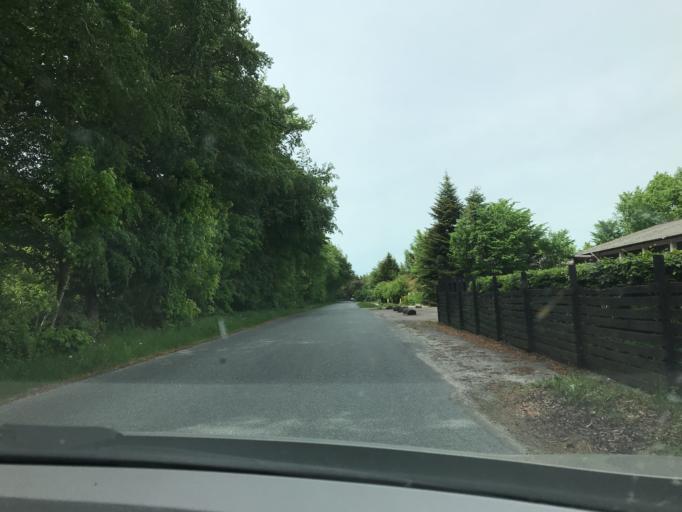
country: DK
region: Central Jutland
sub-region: Norddjurs Kommune
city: Allingabro
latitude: 56.6005
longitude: 10.3104
